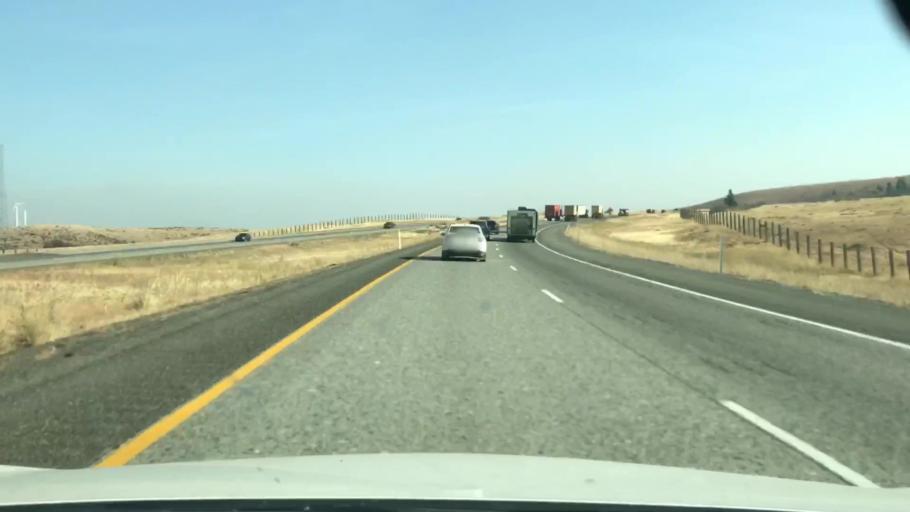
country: US
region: Washington
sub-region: Kittitas County
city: Cle Elum
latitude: 47.1060
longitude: -120.7662
